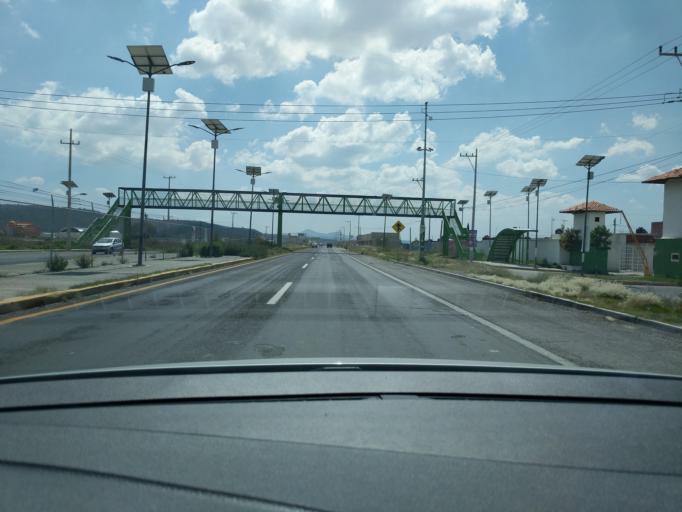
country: MX
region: Hidalgo
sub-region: Mineral de la Reforma
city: Rinconada de los Angeles
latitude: 20.0172
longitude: -98.7205
